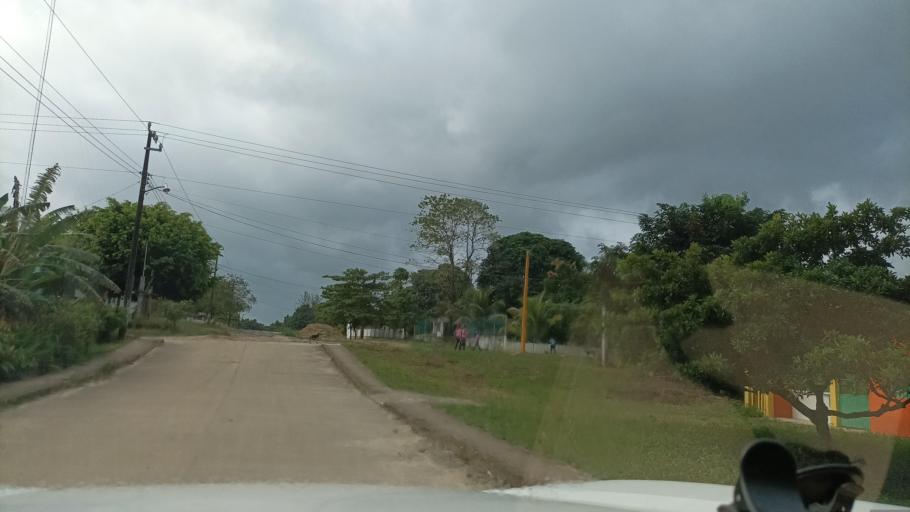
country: MX
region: Veracruz
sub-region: Moloacan
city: Cuichapa
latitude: 17.9236
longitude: -94.3683
